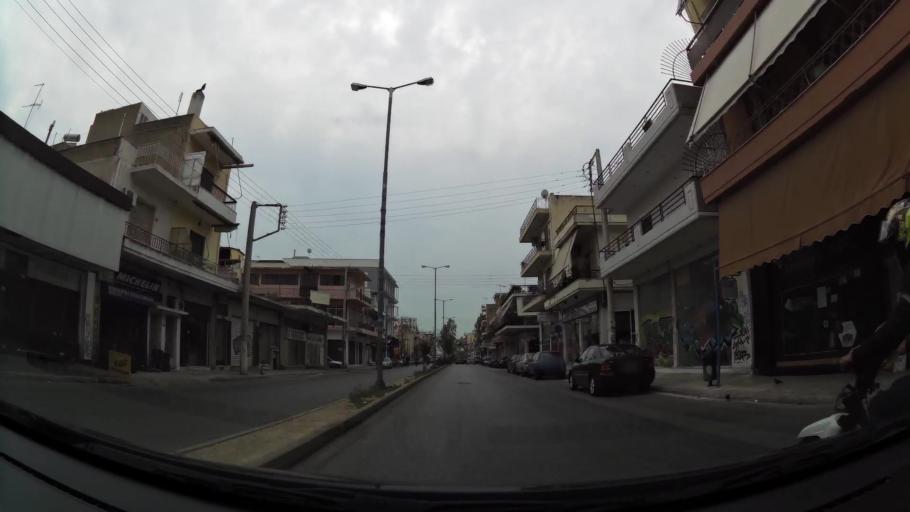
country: GR
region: Attica
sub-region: Nomos Piraios
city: Agios Ioannis Rentis
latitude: 37.9649
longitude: 23.6594
